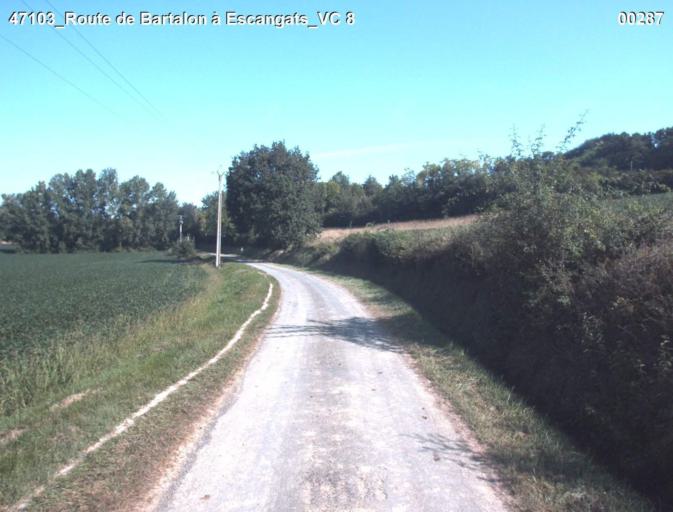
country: FR
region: Aquitaine
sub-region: Departement du Lot-et-Garonne
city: Nerac
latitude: 44.0919
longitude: 0.3167
